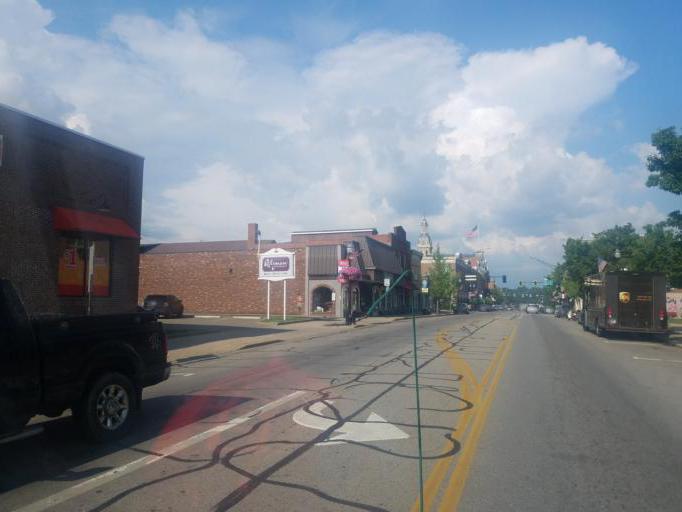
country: US
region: Ohio
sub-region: Wayne County
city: Wooster
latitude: 40.7977
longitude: -81.9428
